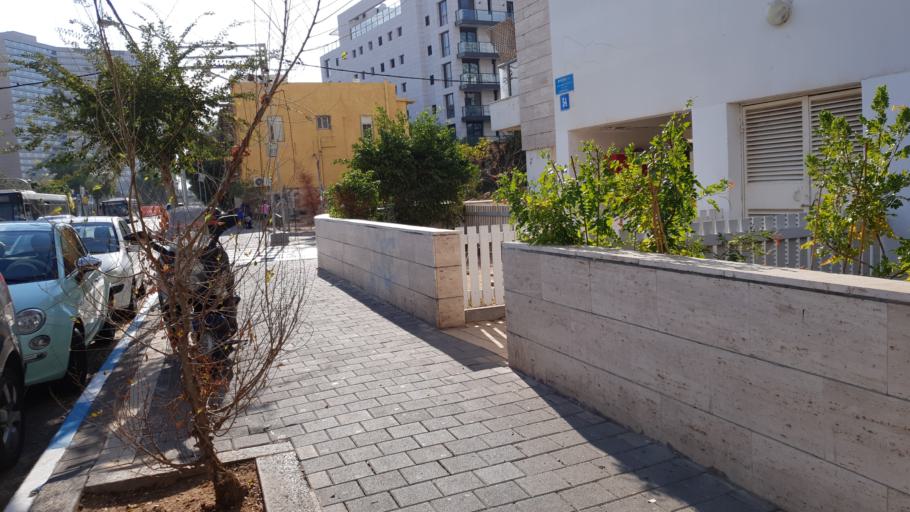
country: IL
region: Tel Aviv
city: Tel Aviv
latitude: 32.0684
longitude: 34.7653
